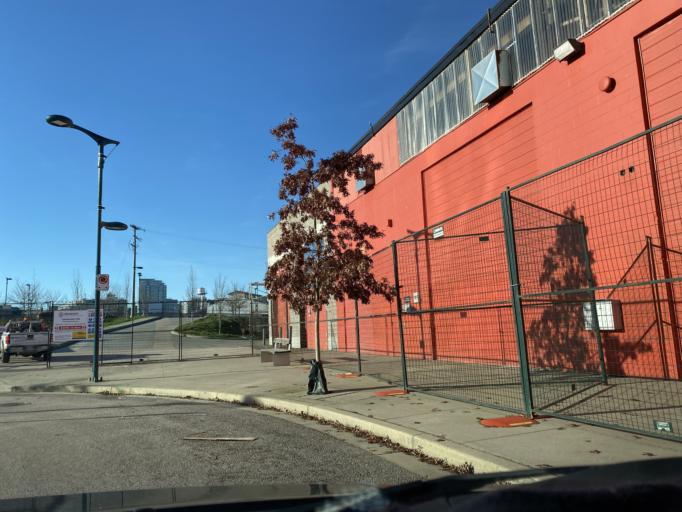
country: CA
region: British Columbia
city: Vancouver
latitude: 49.2680
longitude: -123.0934
